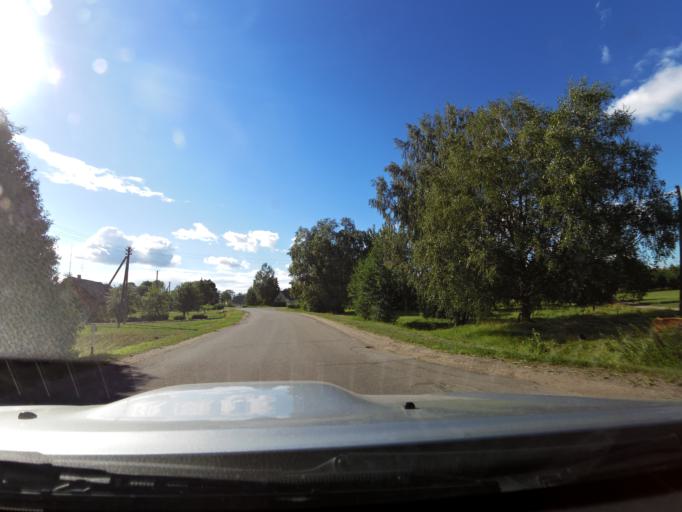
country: LT
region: Panevezys
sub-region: Birzai
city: Birzai
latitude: 56.2449
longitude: 24.8550
